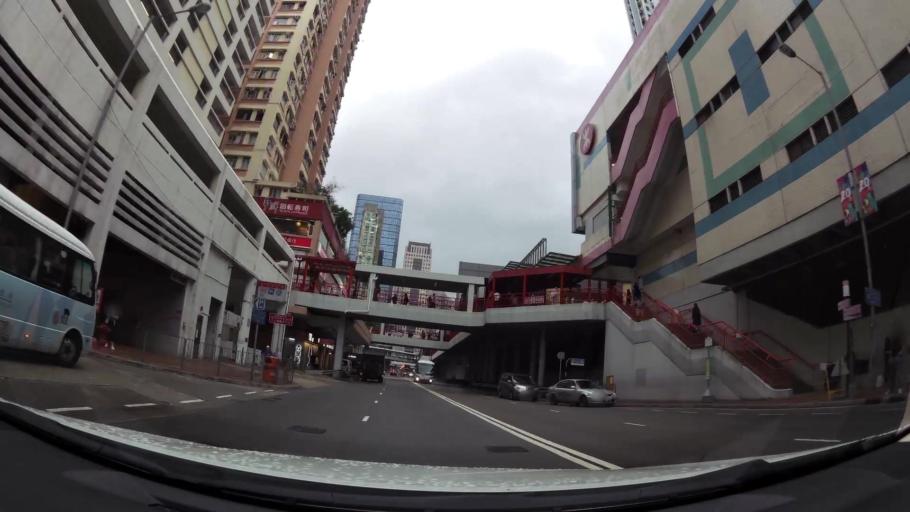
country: HK
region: Tsuen Wan
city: Tsuen Wan
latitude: 22.3729
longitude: 114.1189
